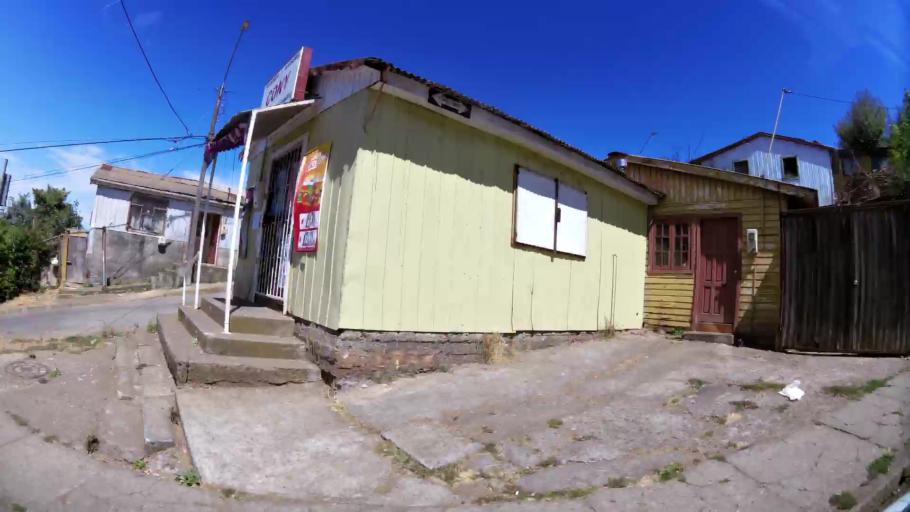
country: CL
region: Biobio
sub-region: Provincia de Concepcion
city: Talcahuano
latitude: -36.7161
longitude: -73.1227
